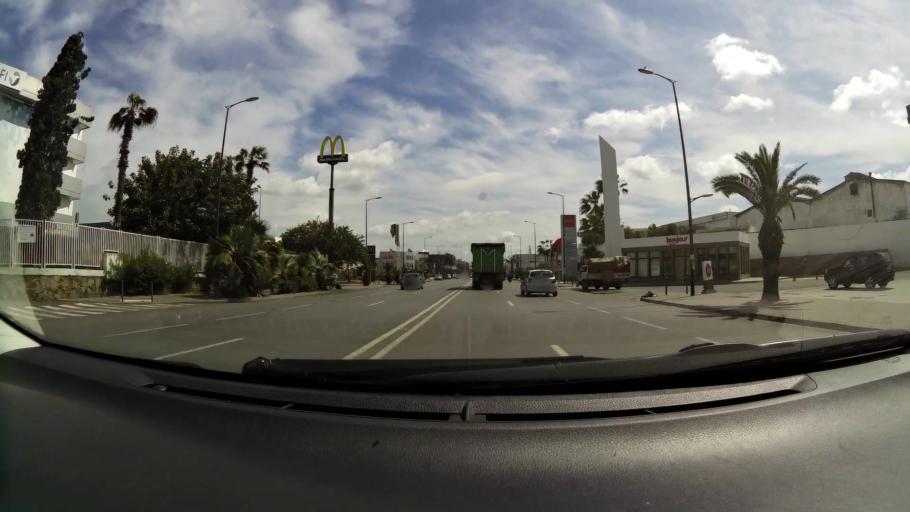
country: MA
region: Grand Casablanca
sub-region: Casablanca
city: Casablanca
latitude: 33.6032
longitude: -7.5498
